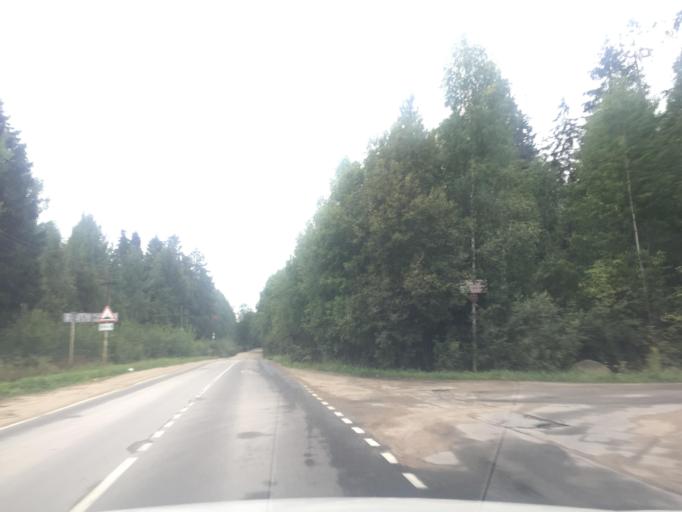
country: RU
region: Leningrad
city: Siverskiy
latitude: 59.3002
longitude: 30.0353
